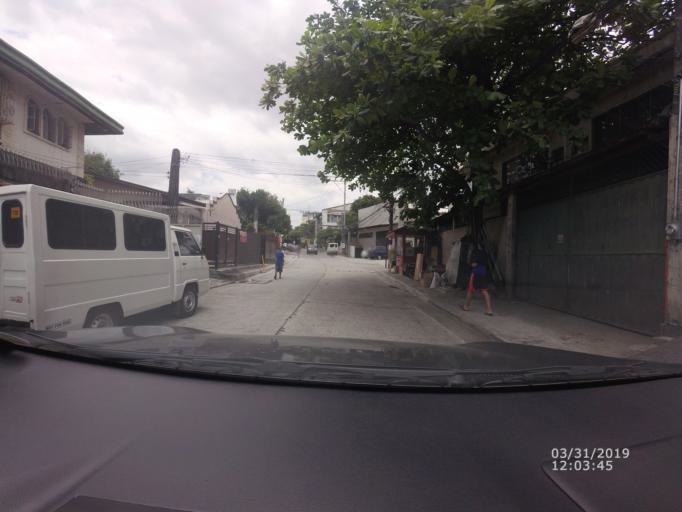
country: PH
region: Metro Manila
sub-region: Mandaluyong
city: Mandaluyong City
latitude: 14.5778
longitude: 121.0368
